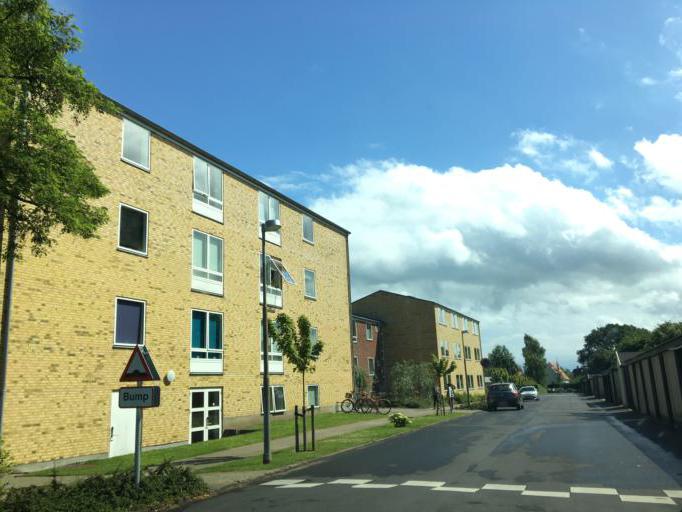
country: DK
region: South Denmark
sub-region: Middelfart Kommune
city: Middelfart
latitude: 55.5006
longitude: 9.7188
